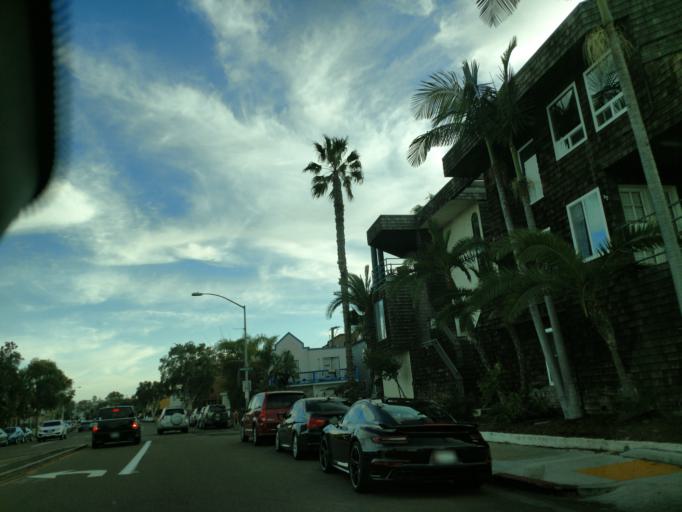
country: US
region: California
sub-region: San Diego County
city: La Jolla
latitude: 32.7639
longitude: -117.2514
